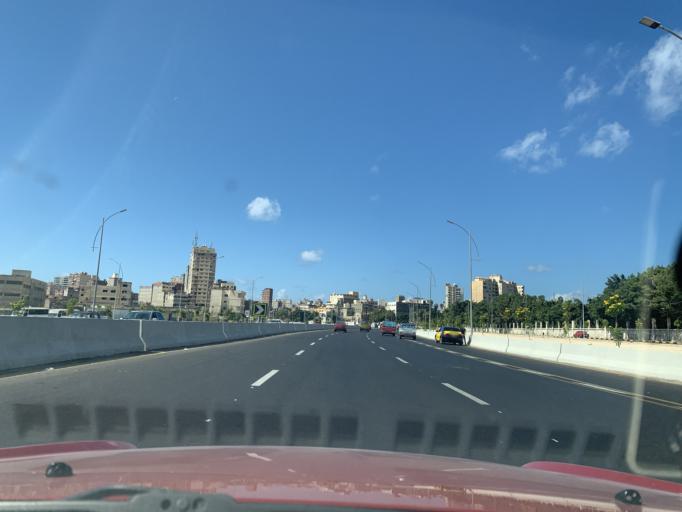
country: EG
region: Alexandria
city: Alexandria
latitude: 31.2010
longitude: 29.9457
